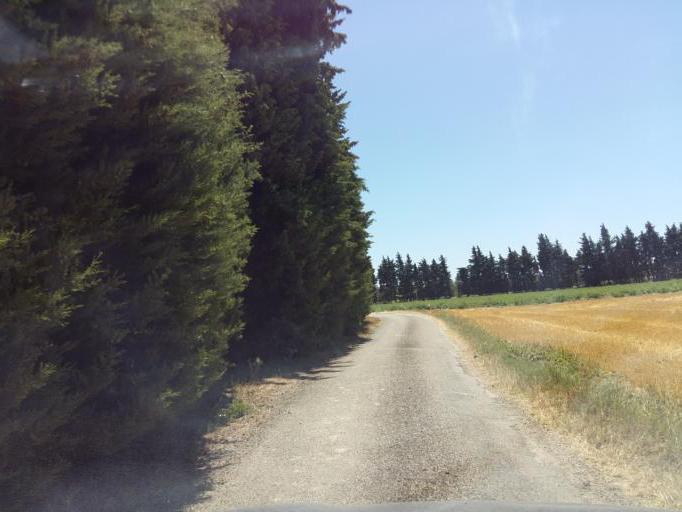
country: FR
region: Provence-Alpes-Cote d'Azur
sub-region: Departement du Vaucluse
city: Orange
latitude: 44.1548
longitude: 4.7872
